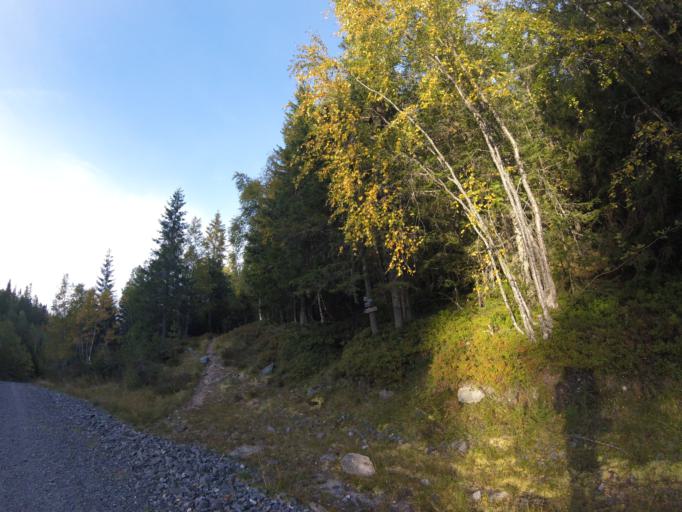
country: NO
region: Buskerud
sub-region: Flesberg
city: Lampeland
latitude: 59.6800
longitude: 9.4349
